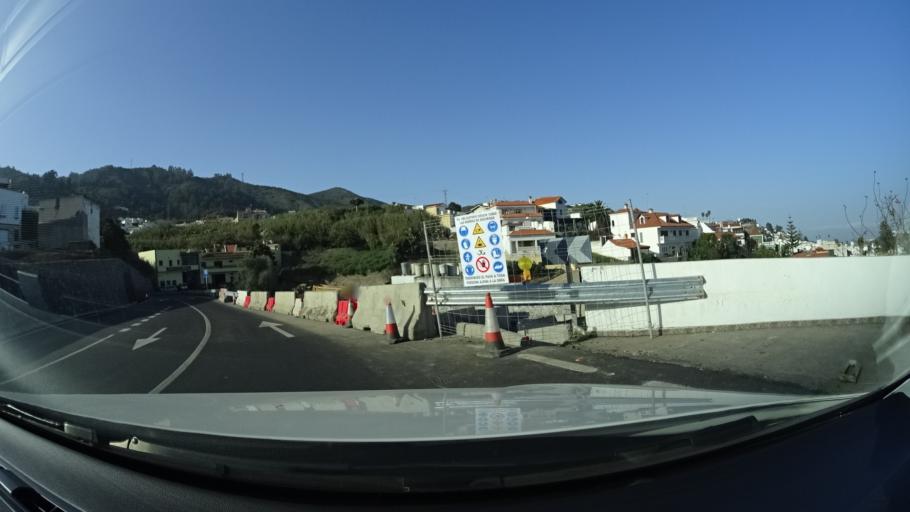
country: ES
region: Canary Islands
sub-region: Provincia de Las Palmas
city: Teror
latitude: 28.0579
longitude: -15.5512
